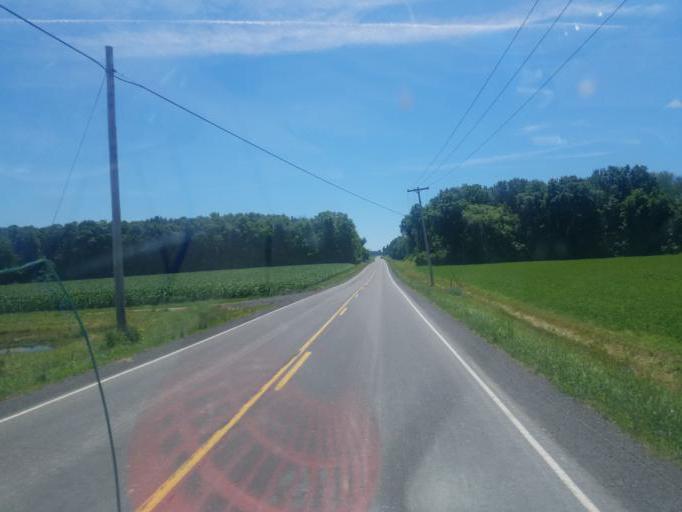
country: US
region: New York
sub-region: Yates County
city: Penn Yan
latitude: 42.6287
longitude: -76.9992
